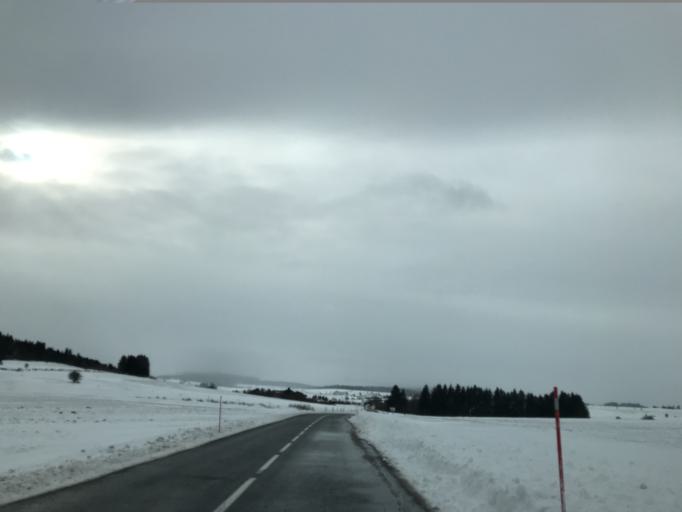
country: FR
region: Auvergne
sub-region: Departement du Puy-de-Dome
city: Aydat
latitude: 45.6656
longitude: 2.9338
